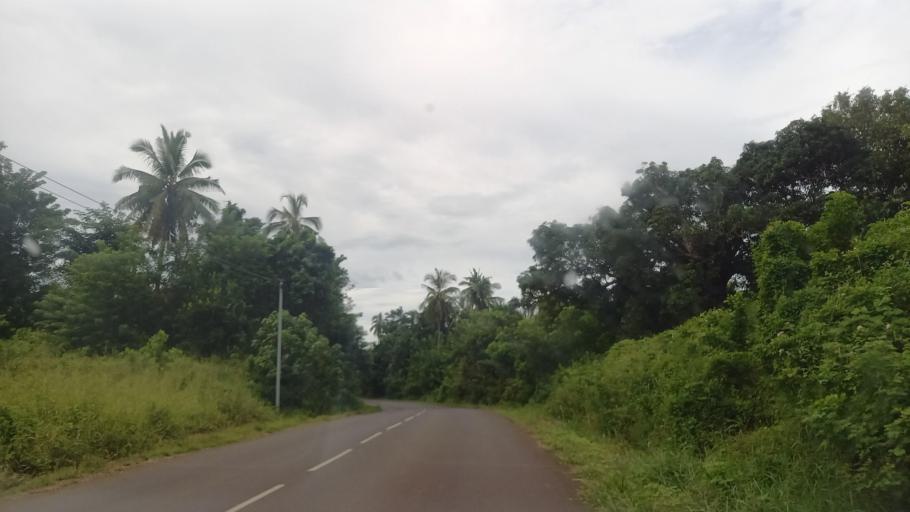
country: YT
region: Boueni
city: Boueni
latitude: -12.9098
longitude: 45.1010
